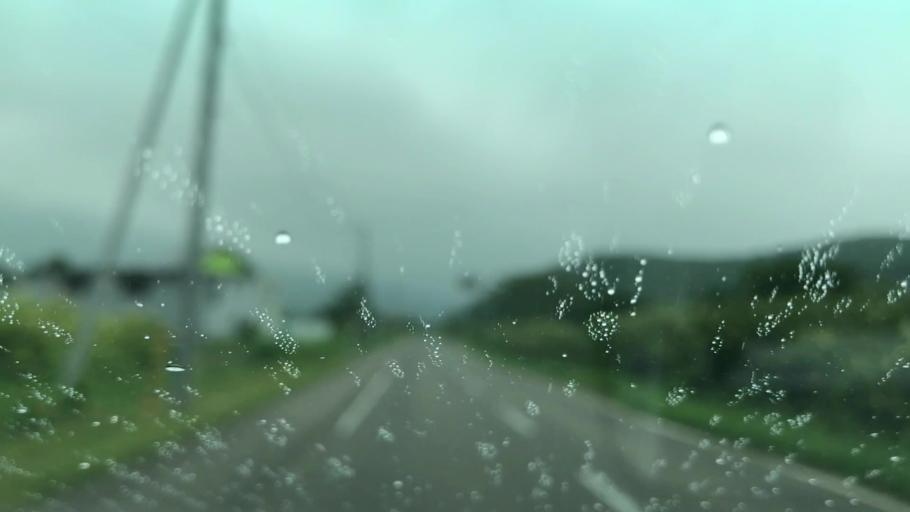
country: JP
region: Hokkaido
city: Iwanai
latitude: 42.7483
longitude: 140.2849
